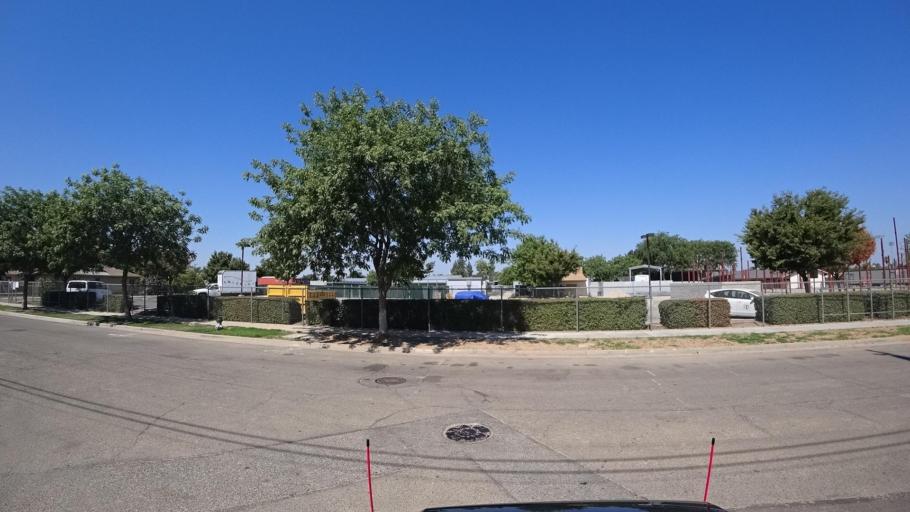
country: US
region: California
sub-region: Fresno County
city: Fresno
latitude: 36.7605
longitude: -119.7770
